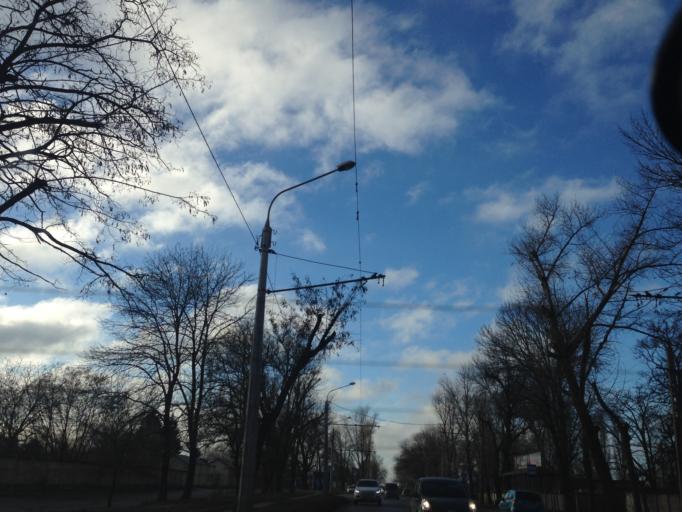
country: RU
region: Rostov
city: Severnyy
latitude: 47.2576
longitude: 39.6369
